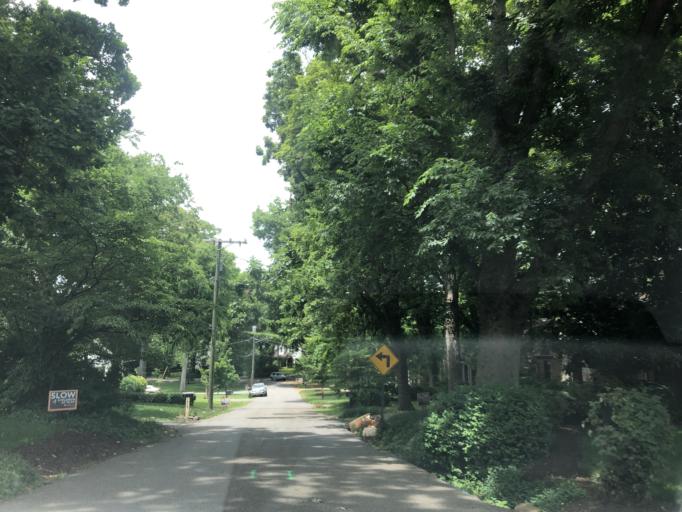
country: US
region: Tennessee
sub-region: Davidson County
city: Oak Hill
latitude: 36.1037
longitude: -86.8042
